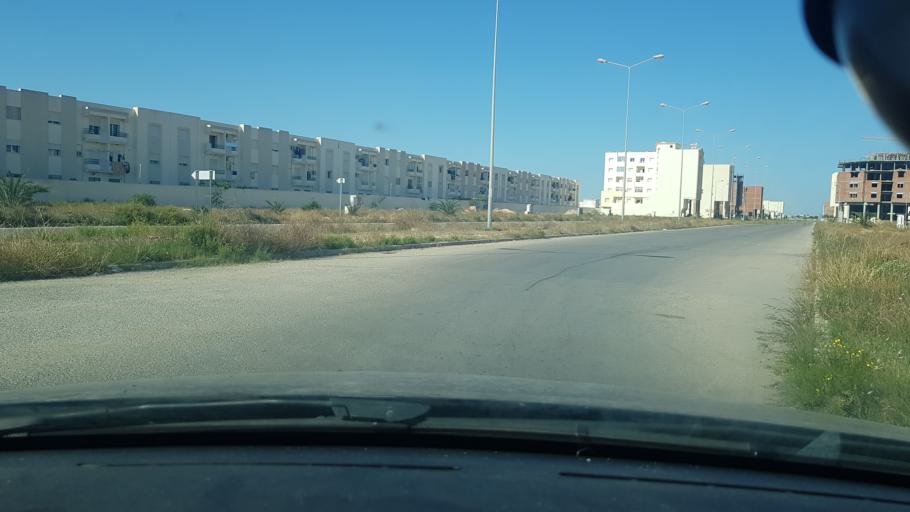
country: TN
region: Safaqis
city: Al Qarmadah
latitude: 34.8318
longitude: 10.7563
